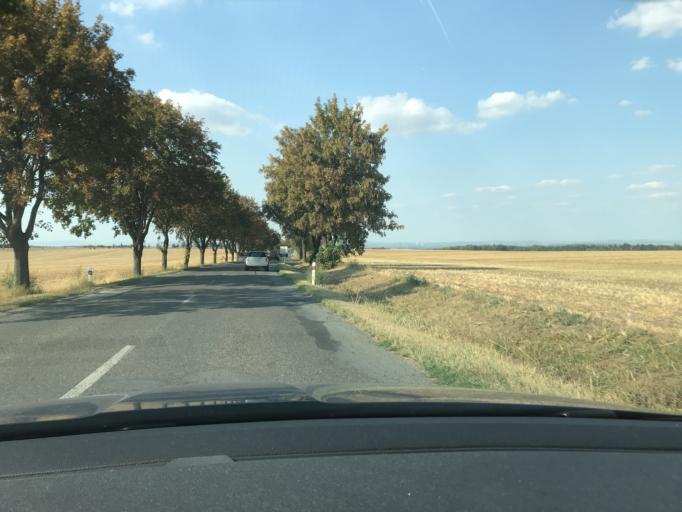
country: CZ
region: Central Bohemia
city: Kralupy nad Vltavou
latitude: 50.2025
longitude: 14.3151
